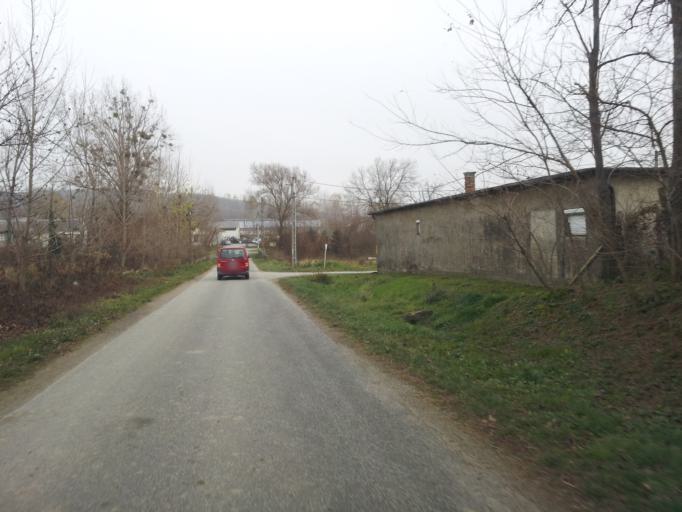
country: HU
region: Zala
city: Cserszegtomaj
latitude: 46.8415
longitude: 17.2244
